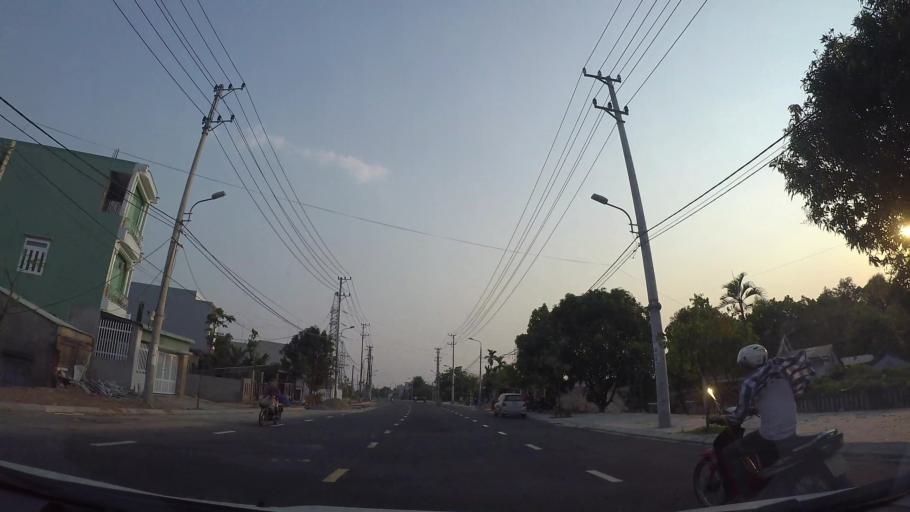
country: VN
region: Da Nang
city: Ngu Hanh Son
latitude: 15.9723
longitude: 108.2320
